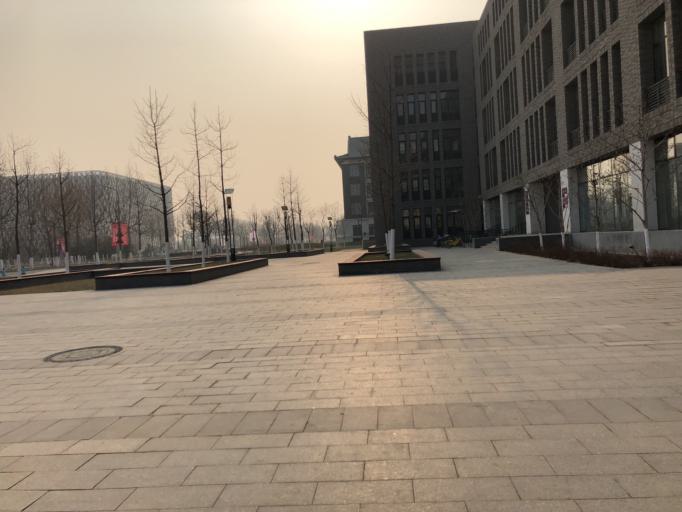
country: CN
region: Beijing
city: Daxing
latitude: 39.7468
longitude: 116.2799
